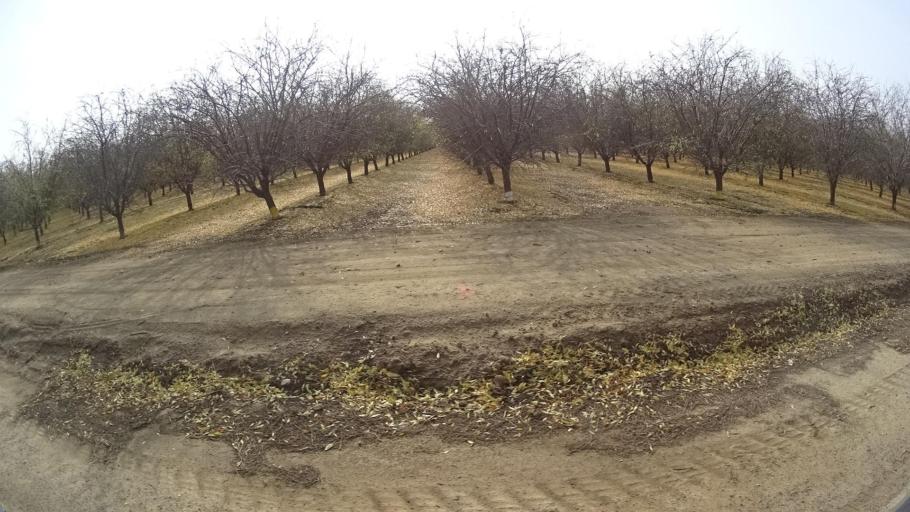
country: US
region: California
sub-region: Kern County
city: Weedpatch
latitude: 35.0763
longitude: -119.0042
